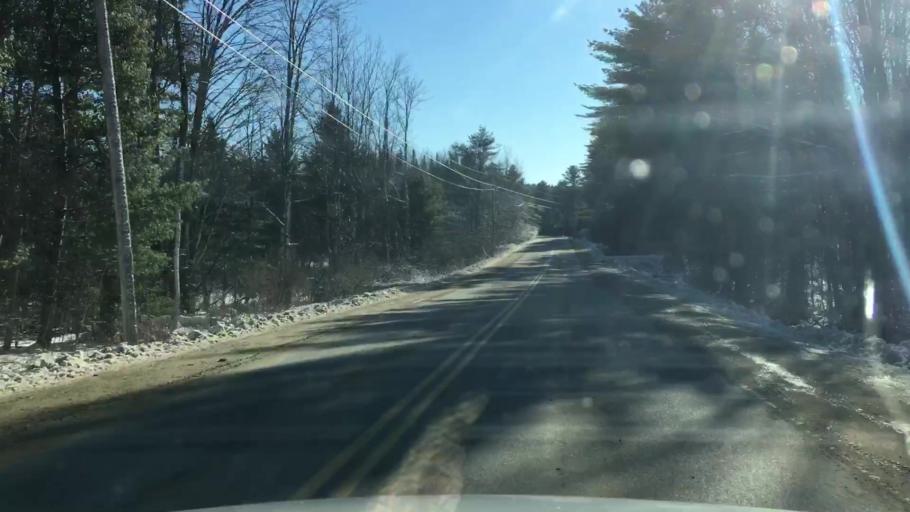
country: US
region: Maine
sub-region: Kennebec County
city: Readfield
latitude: 44.3582
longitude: -69.9911
